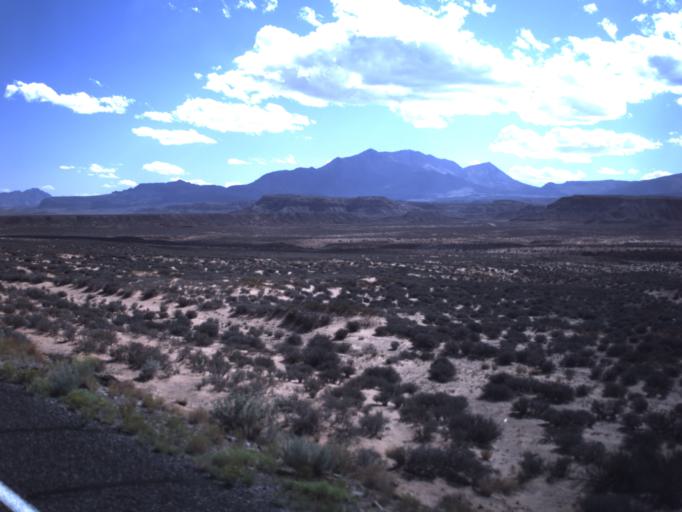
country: US
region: Utah
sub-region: Wayne County
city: Loa
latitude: 38.0867
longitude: -110.6158
